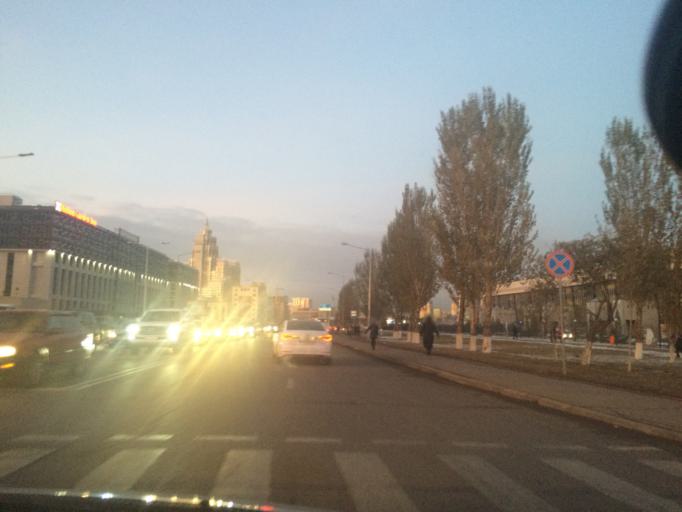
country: KZ
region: Astana Qalasy
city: Astana
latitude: 51.1335
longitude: 71.4146
